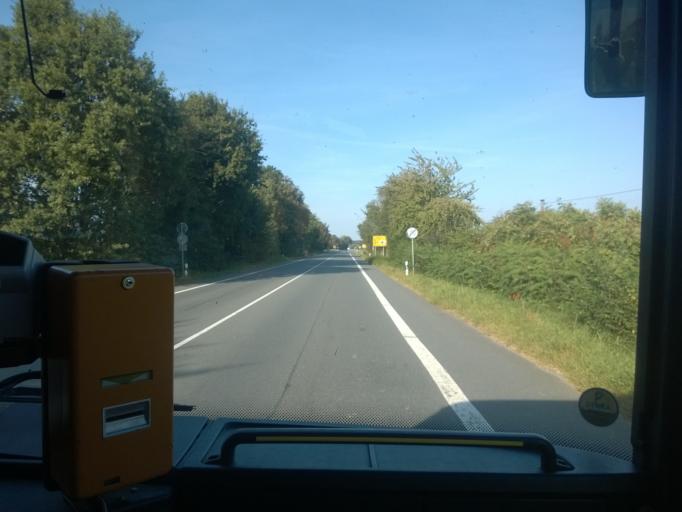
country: DE
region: North Rhine-Westphalia
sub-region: Regierungsbezirk Munster
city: Sudlohn
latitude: 51.9336
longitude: 6.8554
